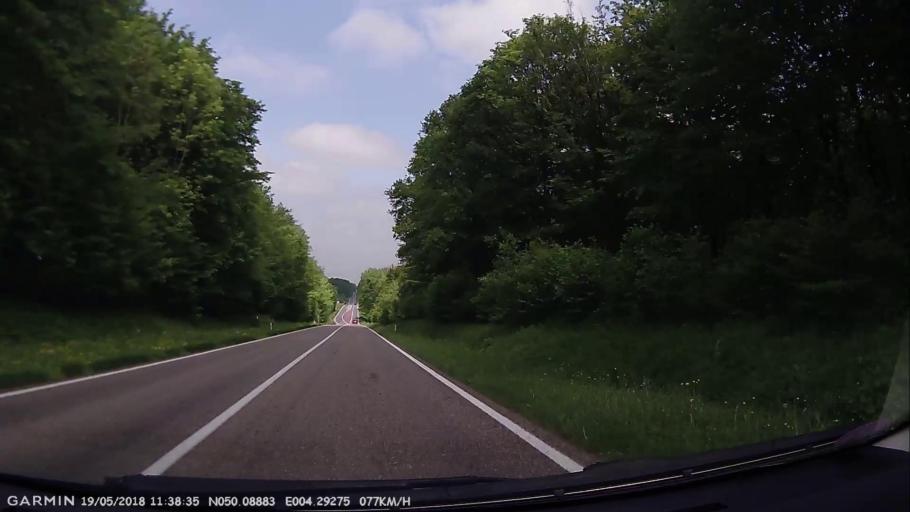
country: BE
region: Wallonia
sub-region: Province du Hainaut
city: Chimay
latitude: 50.0891
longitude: 4.2926
